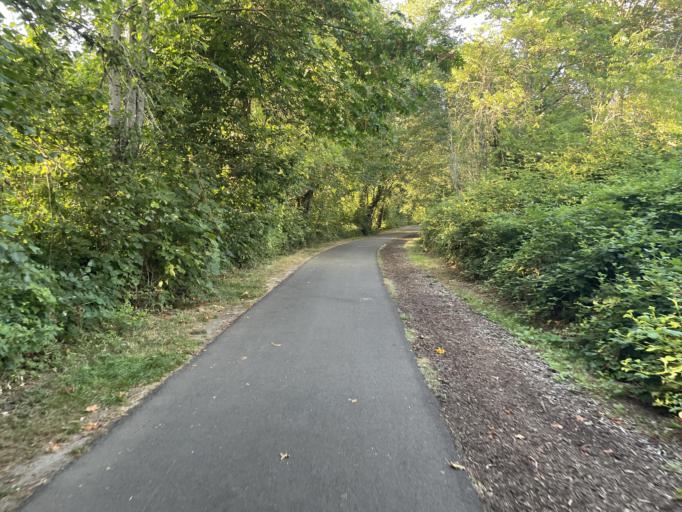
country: US
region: Oregon
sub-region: Marion County
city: Salem
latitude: 44.9214
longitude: -123.0751
